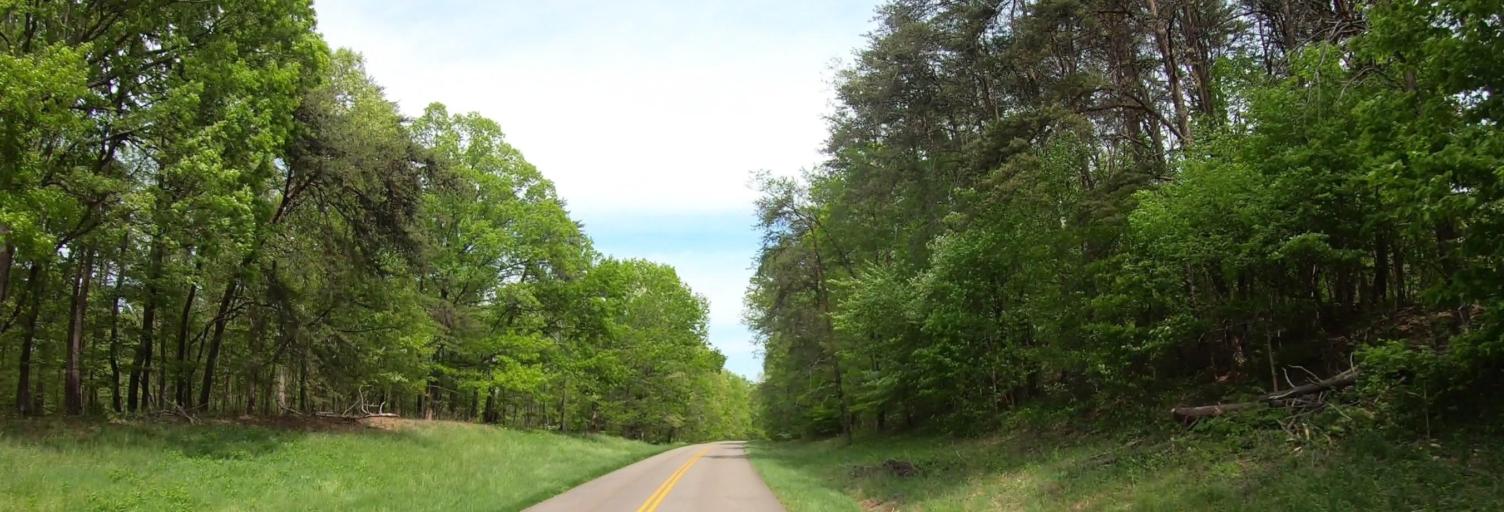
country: US
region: Virginia
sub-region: Roanoke County
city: Vinton
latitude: 37.2386
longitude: -79.8939
